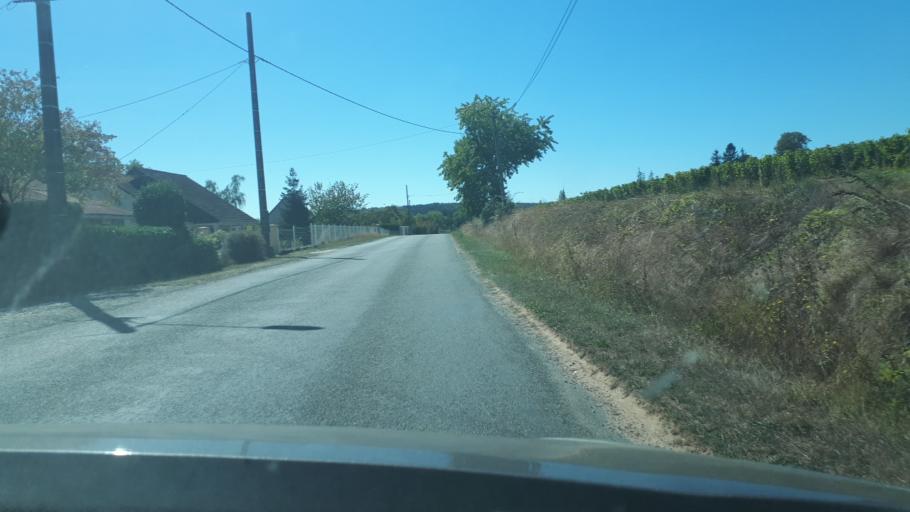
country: FR
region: Centre
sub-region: Departement du Cher
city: Sancerre
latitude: 47.2625
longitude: 2.7643
